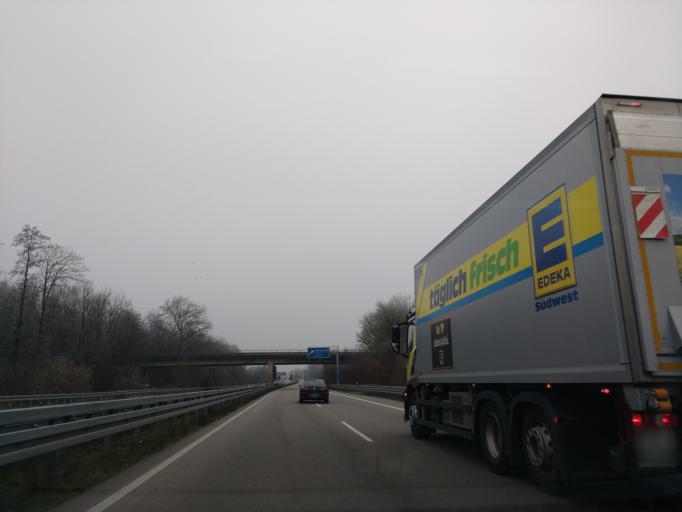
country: DE
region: Baden-Wuerttemberg
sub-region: Freiburg Region
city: Appenweier
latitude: 48.5339
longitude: 7.9441
